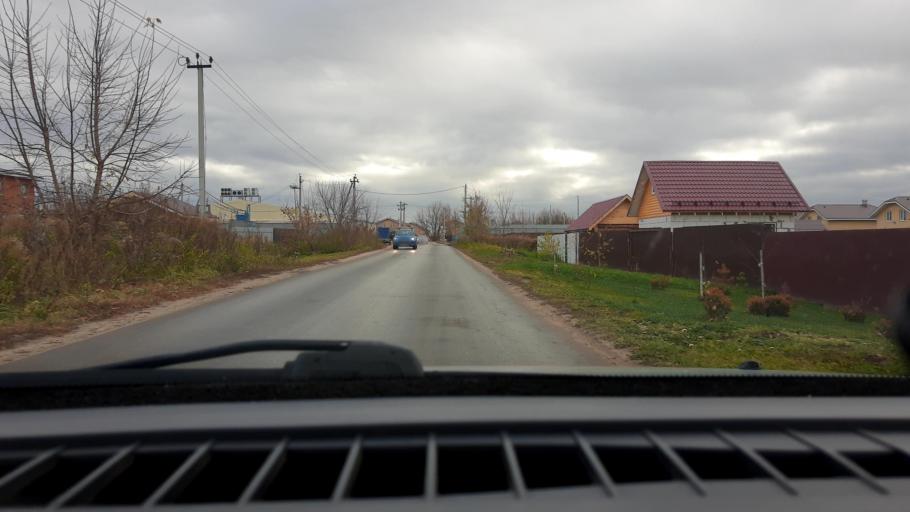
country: RU
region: Nizjnij Novgorod
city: Afonino
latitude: 56.2029
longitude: 44.1321
